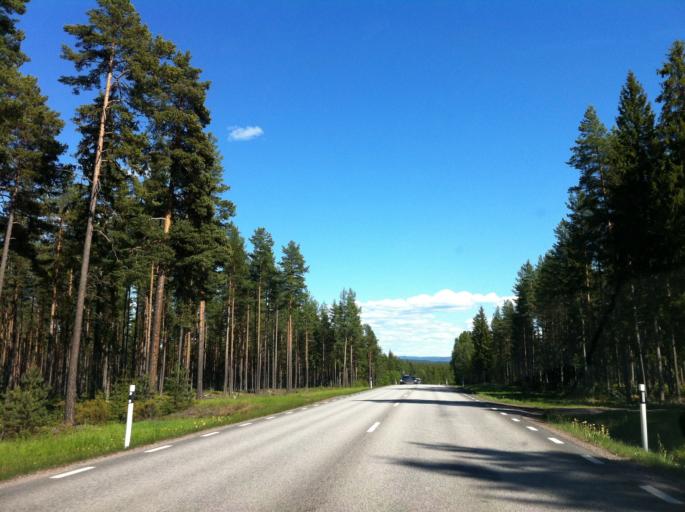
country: SE
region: Dalarna
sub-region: Leksand Municipality
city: Siljansnas
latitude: 60.9217
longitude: 14.8327
